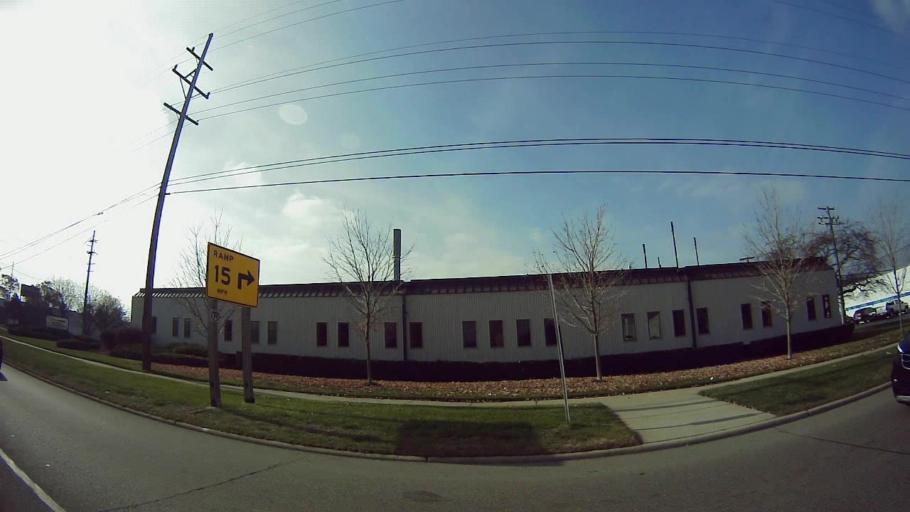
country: US
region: Michigan
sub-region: Oakland County
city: Southfield
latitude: 42.4455
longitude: -83.2783
